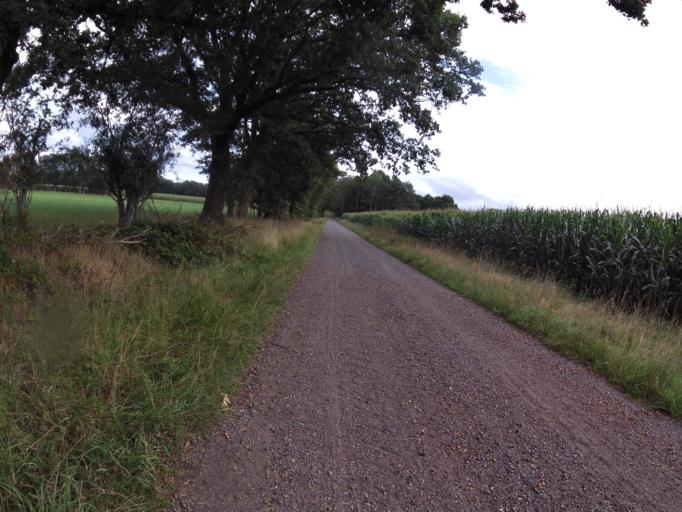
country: DE
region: Lower Saxony
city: Hipstedt
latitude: 53.5014
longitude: 8.9194
